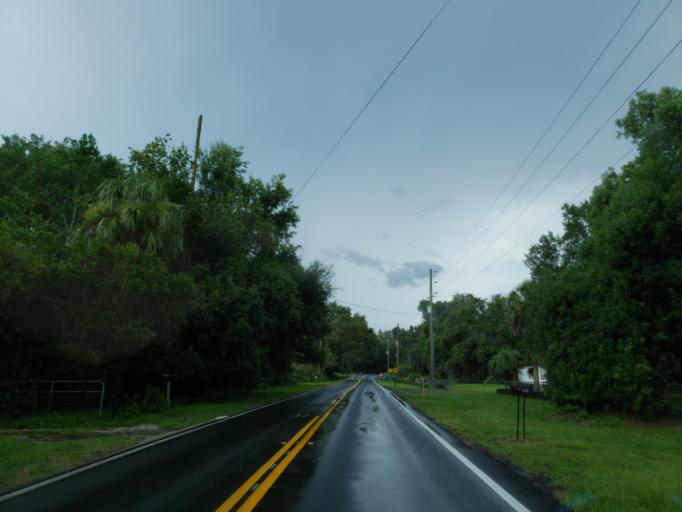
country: US
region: Florida
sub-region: Pasco County
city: Land O' Lakes
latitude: 28.2826
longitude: -82.4359
